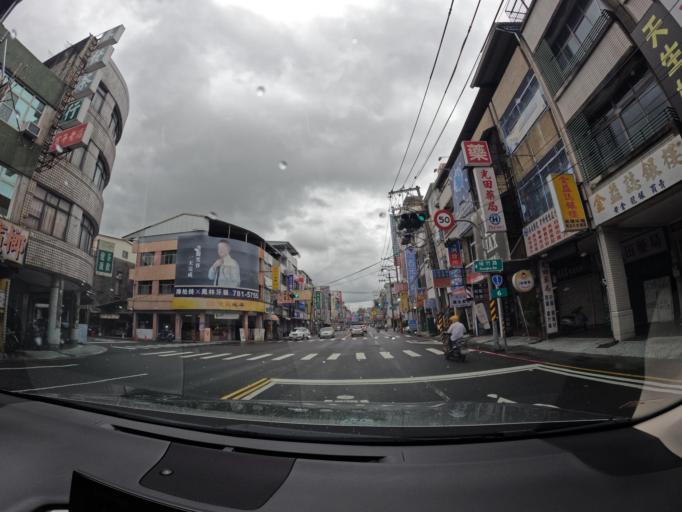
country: TW
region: Taiwan
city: Fengshan
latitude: 22.6242
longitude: 120.3656
